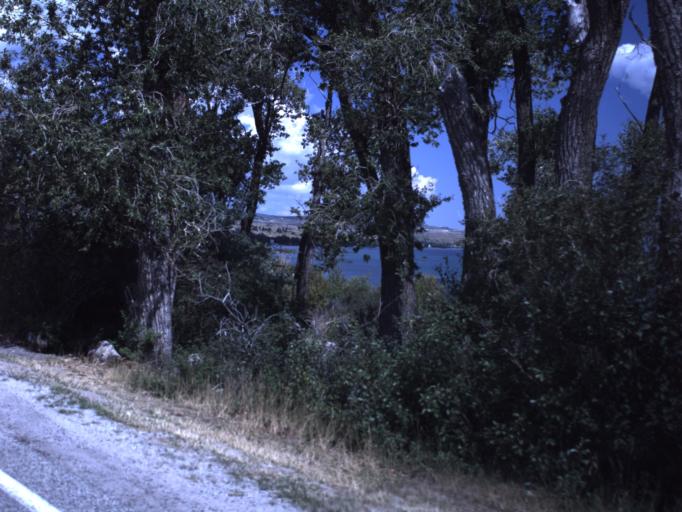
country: US
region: Idaho
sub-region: Bear Lake County
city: Paris
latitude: 41.9798
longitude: -111.4047
